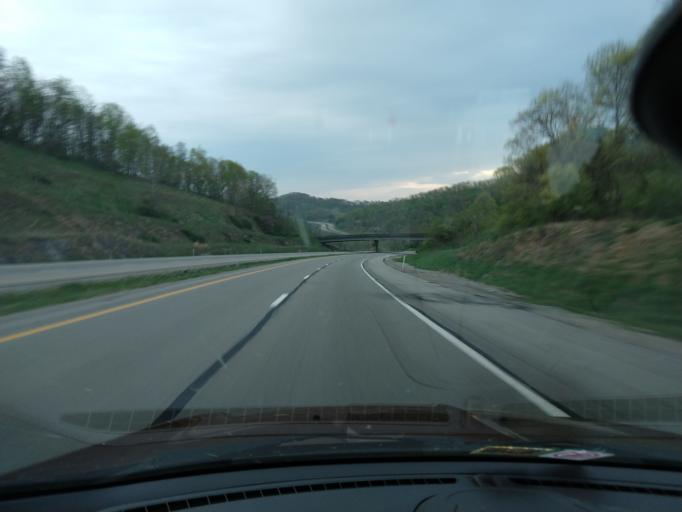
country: US
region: West Virginia
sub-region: Lewis County
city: Weston
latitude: 38.9170
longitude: -80.5694
